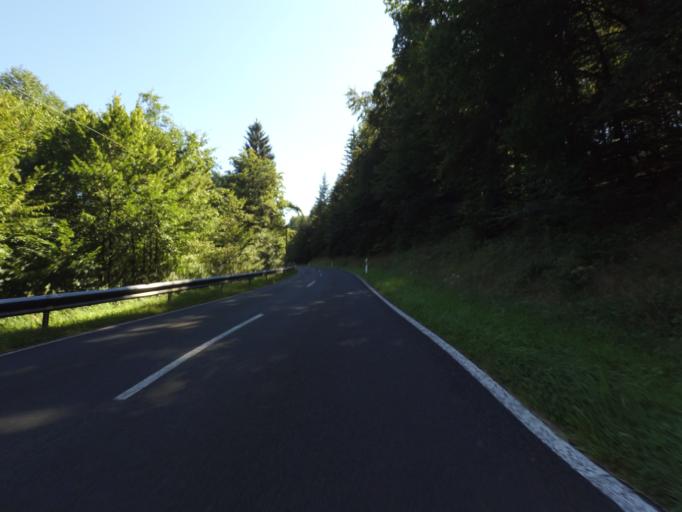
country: DE
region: Rheinland-Pfalz
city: Filz
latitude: 50.1612
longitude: 6.9688
